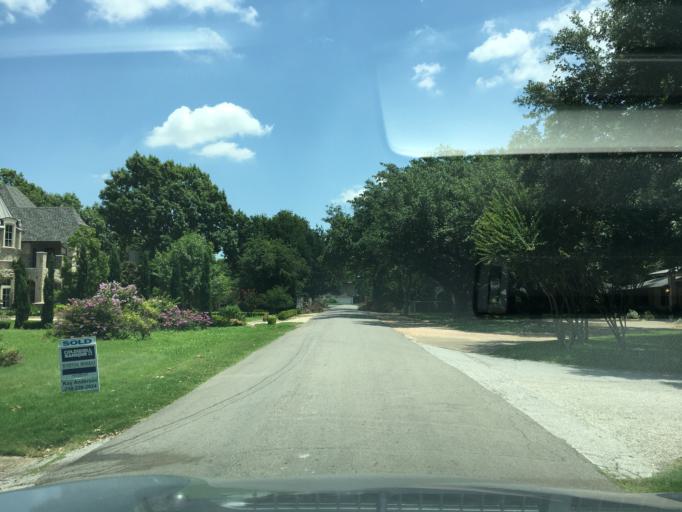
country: US
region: Texas
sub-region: Dallas County
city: University Park
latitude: 32.8839
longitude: -96.8075
